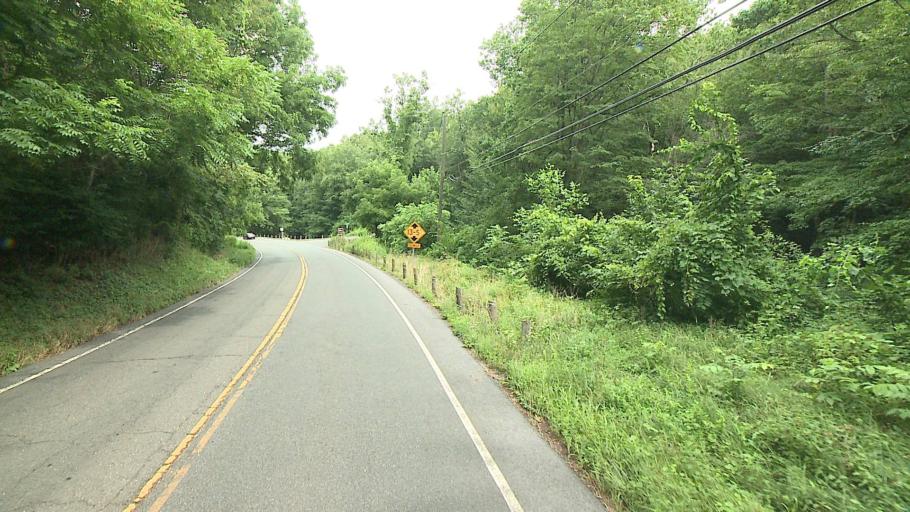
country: US
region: Connecticut
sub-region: Fairfield County
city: Newtown
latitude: 41.4745
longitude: -73.3520
